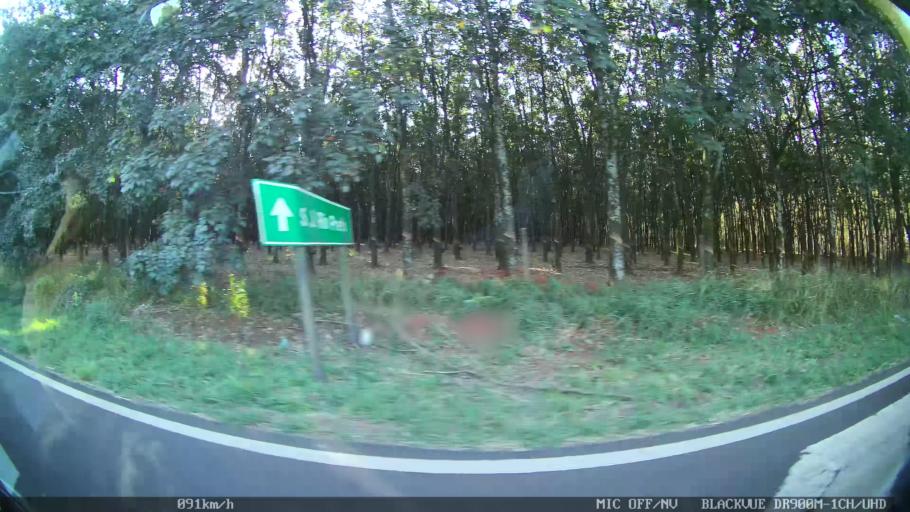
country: BR
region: Sao Paulo
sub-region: Guapiacu
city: Guapiacu
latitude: -20.7611
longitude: -49.1785
